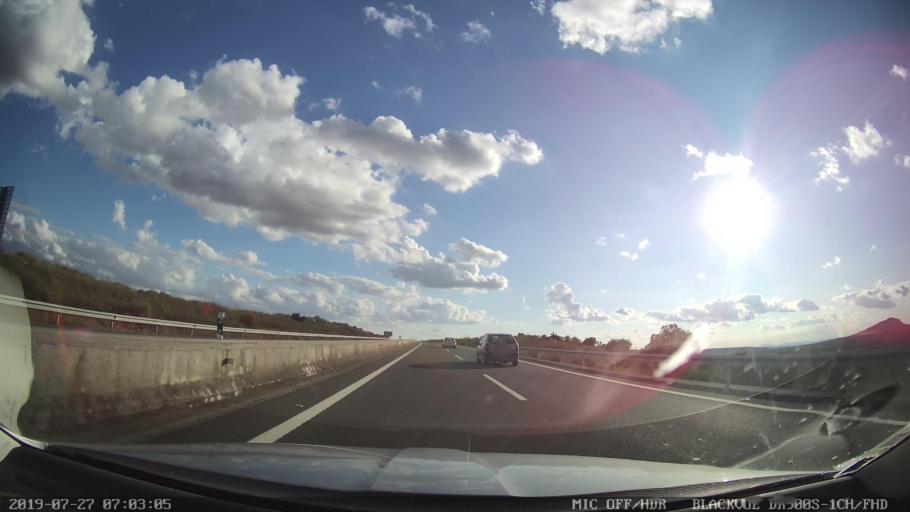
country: ES
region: Extremadura
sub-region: Provincia de Caceres
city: Casas de Miravete
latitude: 39.6800
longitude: -5.7319
